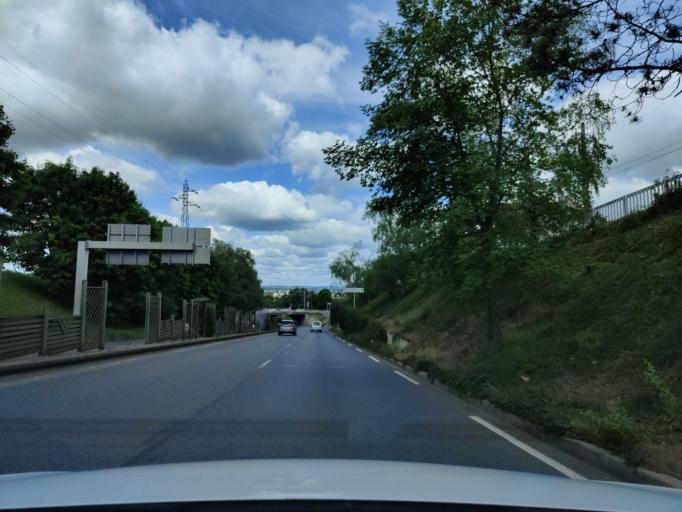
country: FR
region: Auvergne
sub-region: Departement de l'Allier
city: Desertines
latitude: 46.3453
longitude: 2.6118
